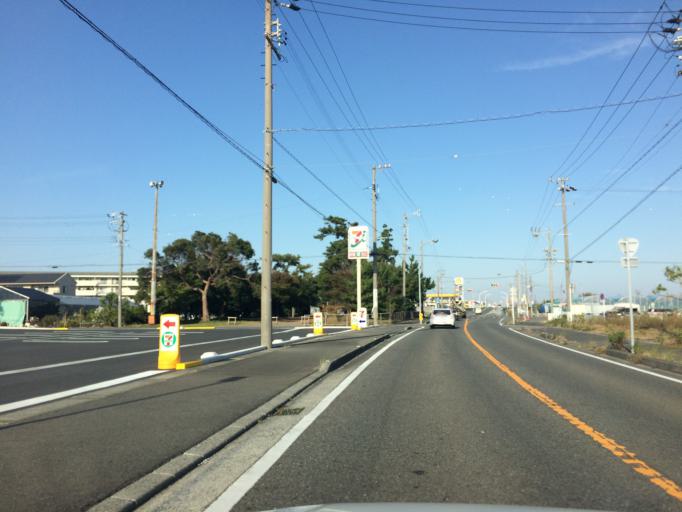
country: JP
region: Shizuoka
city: Sagara
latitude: 34.7255
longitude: 138.2200
